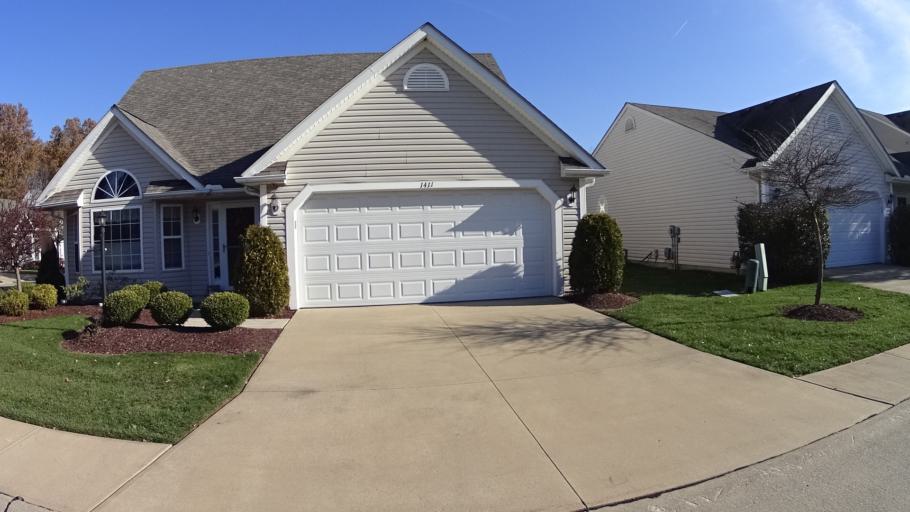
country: US
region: Ohio
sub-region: Lorain County
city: Avon Center
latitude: 41.4703
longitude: -82.0240
